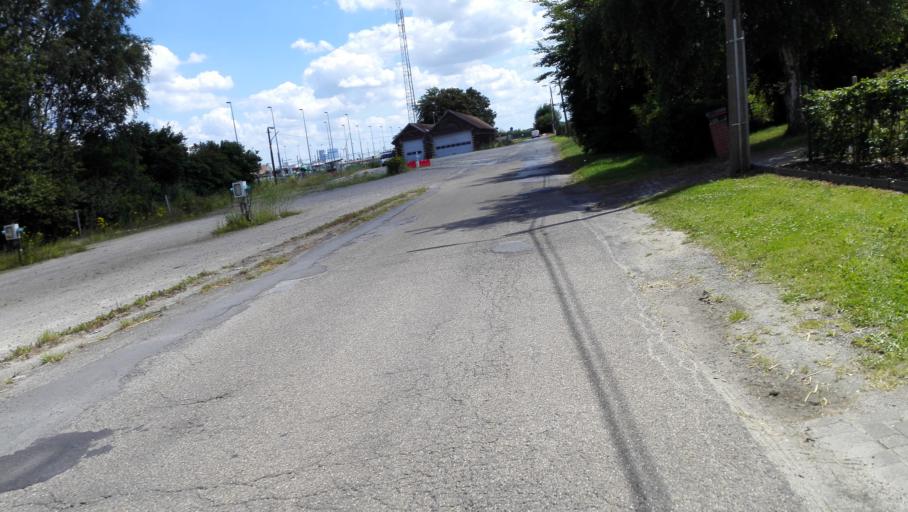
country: BE
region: Flanders
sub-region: Provincie Vlaams-Brabant
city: Tienen
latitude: 50.8092
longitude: 4.9216
